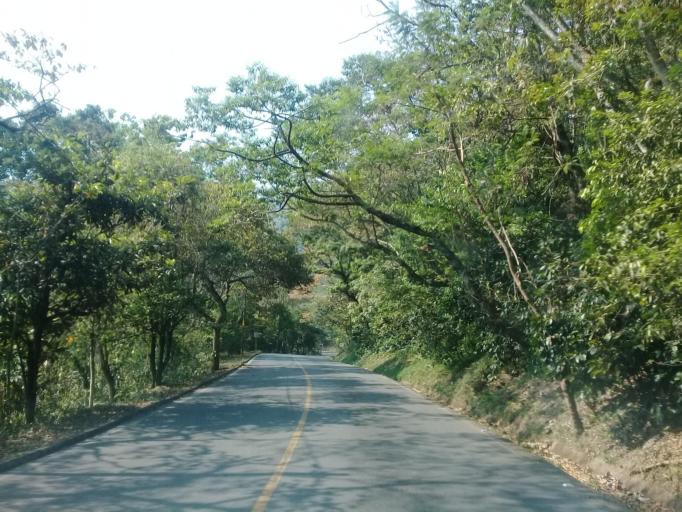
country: MX
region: Veracruz
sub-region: Ixtaczoquitlan
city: Campo Chico
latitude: 18.8414
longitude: -97.0278
